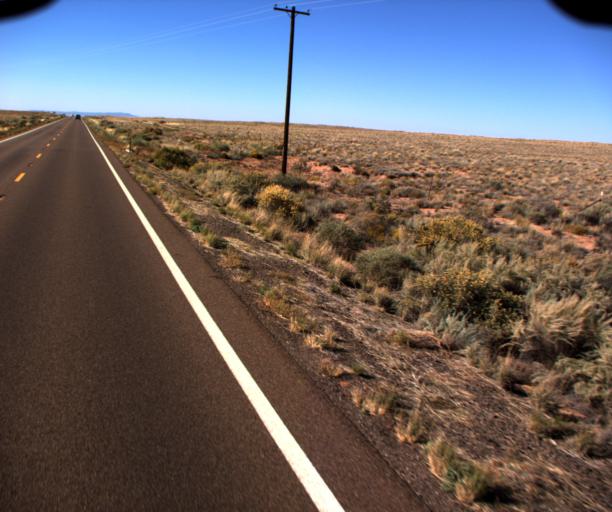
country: US
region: Arizona
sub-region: Navajo County
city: Winslow
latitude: 35.0728
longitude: -110.5693
